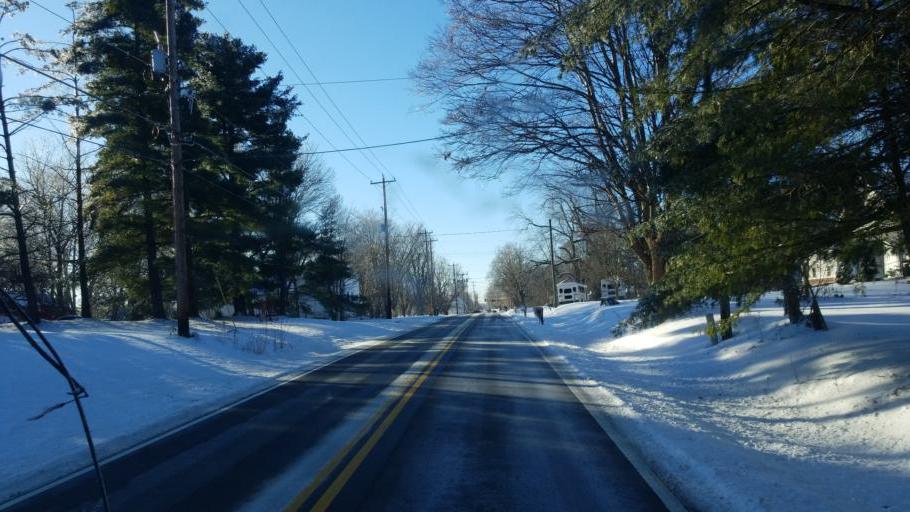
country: US
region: Ohio
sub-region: Delaware County
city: Sunbury
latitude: 40.2684
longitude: -82.9088
